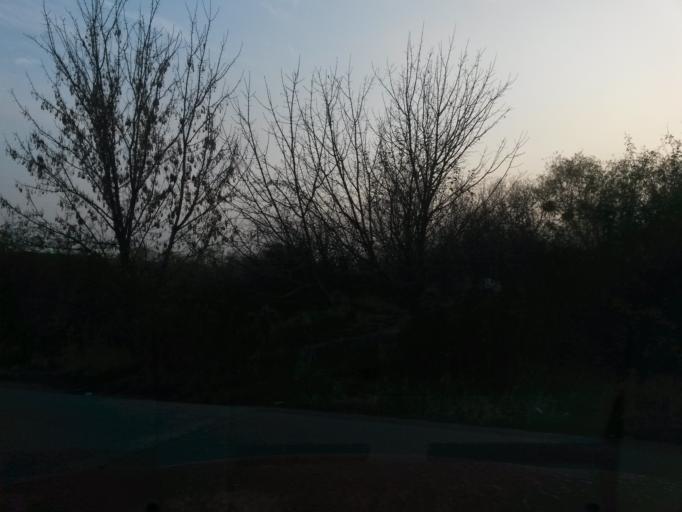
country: SK
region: Kosicky
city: Kosice
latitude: 48.6951
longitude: 21.2474
